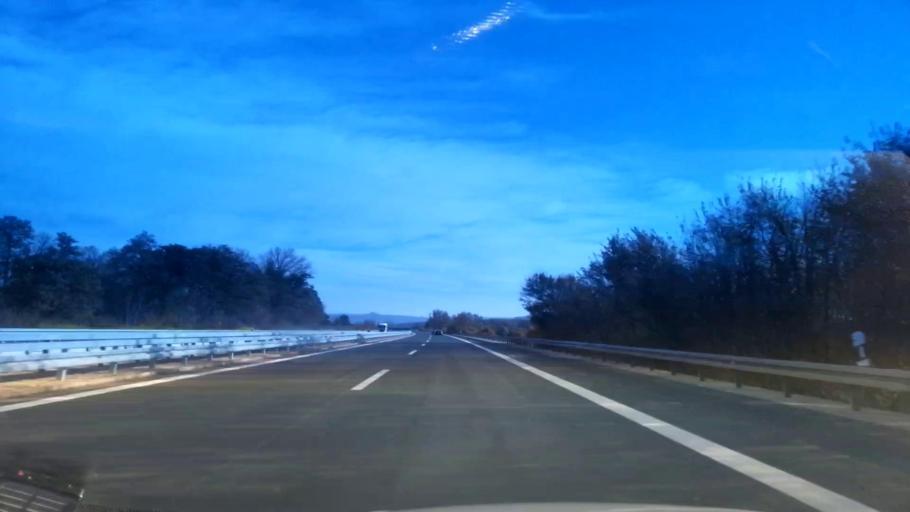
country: DE
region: Bavaria
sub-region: Upper Franconia
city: Gundelsheim
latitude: 49.9329
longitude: 10.9383
